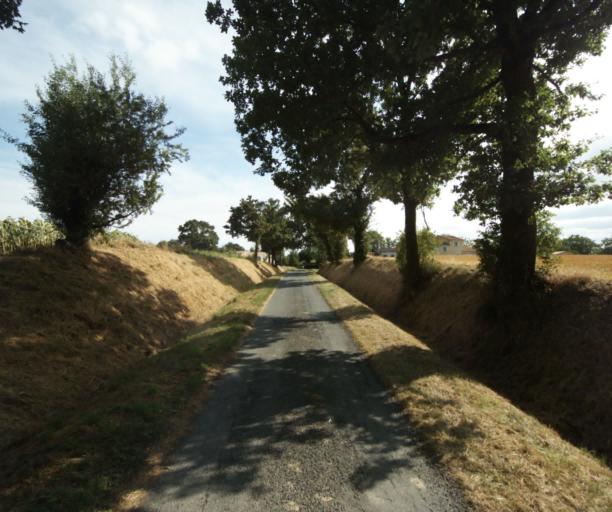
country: FR
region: Midi-Pyrenees
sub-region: Departement du Tarn
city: Puylaurens
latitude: 43.5329
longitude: 1.9827
